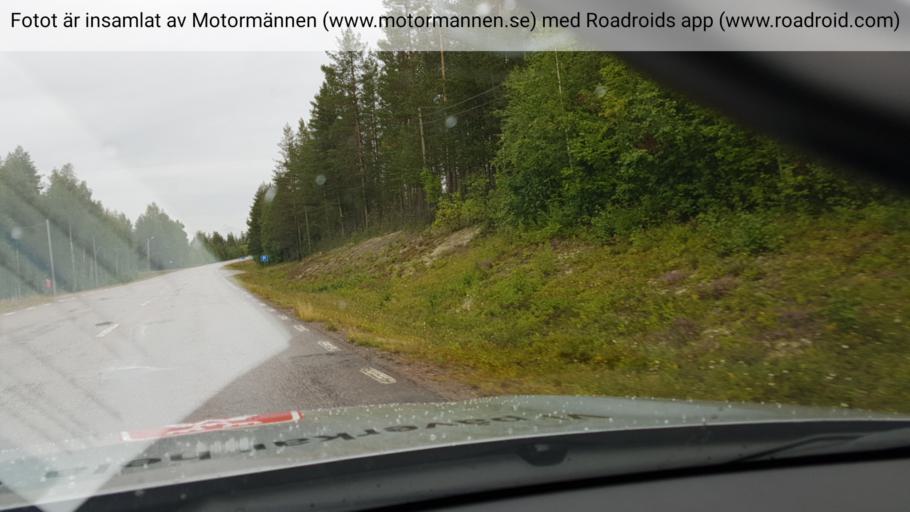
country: SE
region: Norrbotten
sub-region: Alvsbyns Kommun
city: AElvsbyn
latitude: 66.2105
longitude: 20.8755
